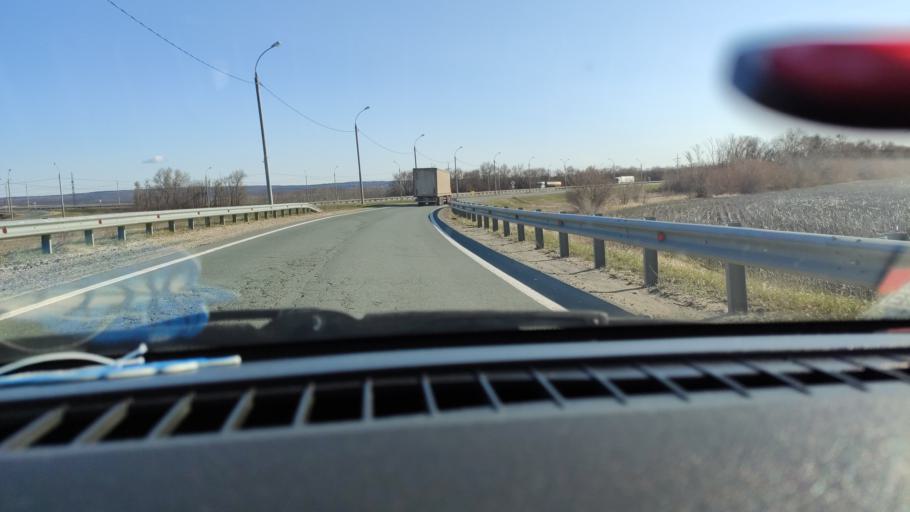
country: RU
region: Samara
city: Varlamovo
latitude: 53.1948
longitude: 48.2943
